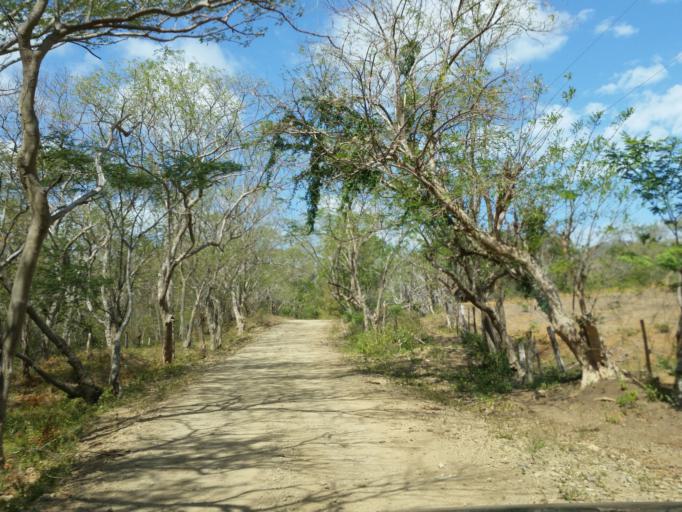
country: CR
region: Guanacaste
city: La Cruz
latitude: 11.1069
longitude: -85.7393
